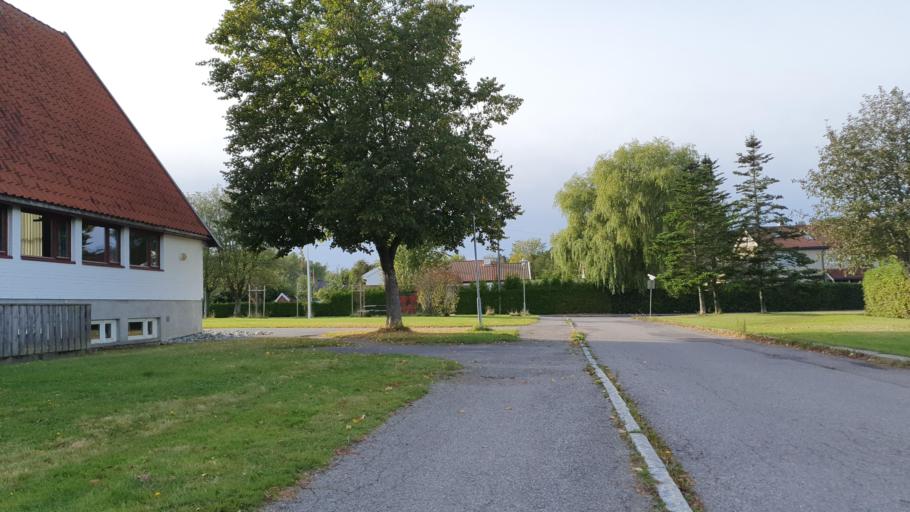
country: NO
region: Vestfold
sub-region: Tonsberg
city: Tonsberg
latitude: 59.2753
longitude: 10.4196
